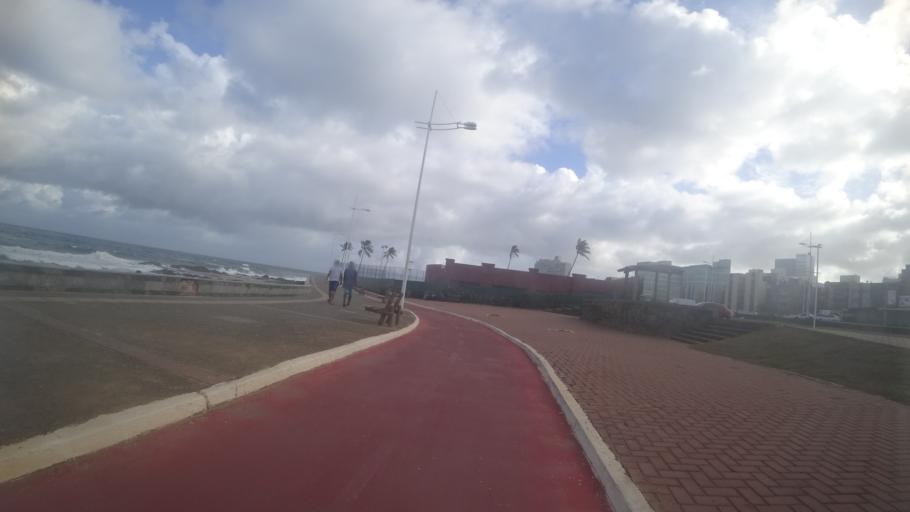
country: BR
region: Bahia
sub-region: Salvador
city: Salvador
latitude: -13.0014
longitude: -38.4498
